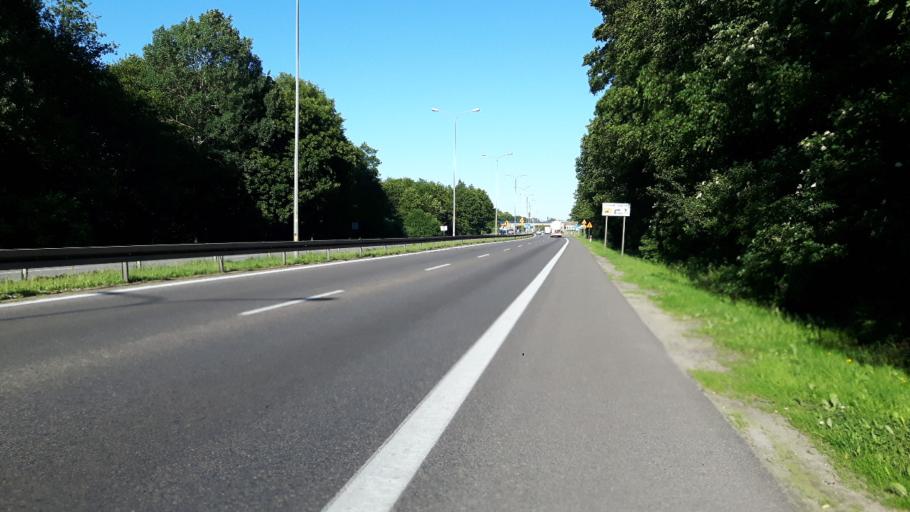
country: PL
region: Pomeranian Voivodeship
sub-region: Powiat wejherowski
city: Reda
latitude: 54.6045
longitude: 18.3336
